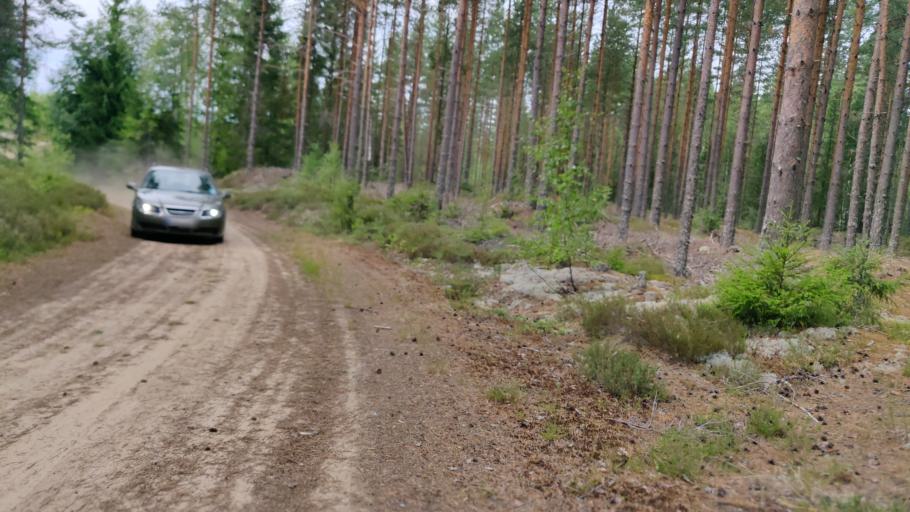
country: SE
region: Vaermland
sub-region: Hagfors Kommun
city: Hagfors
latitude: 60.0169
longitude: 13.5585
